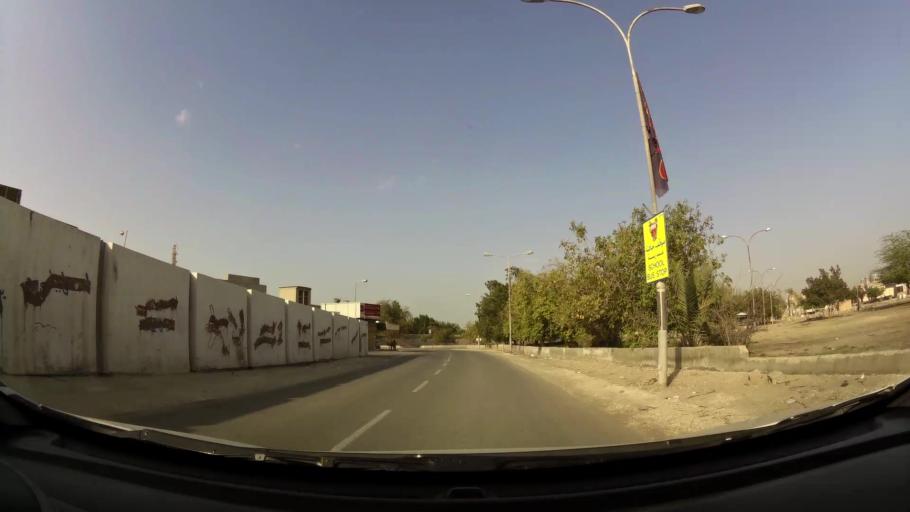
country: BH
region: Manama
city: Jidd Hafs
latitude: 26.2178
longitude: 50.5038
